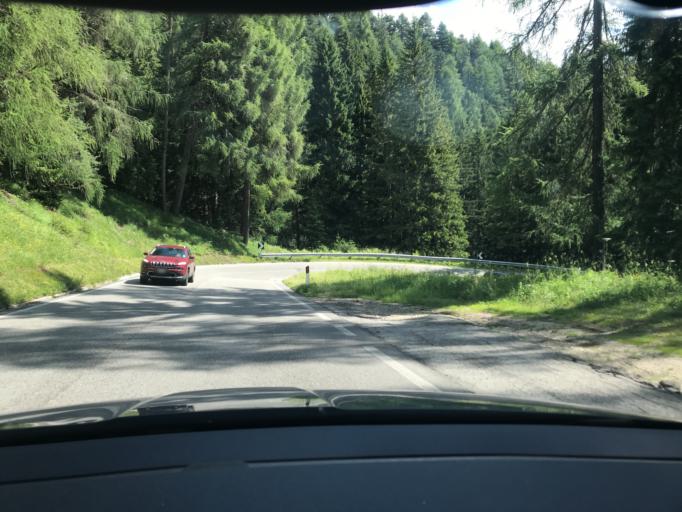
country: IT
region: Veneto
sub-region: Provincia di Belluno
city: Cortina d'Ampezzo
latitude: 46.5226
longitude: 12.1159
